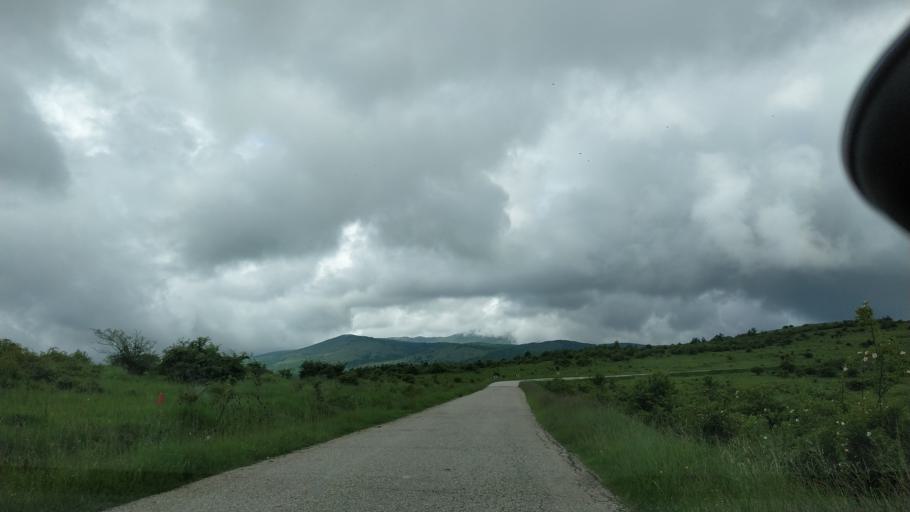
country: RS
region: Central Serbia
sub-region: Zajecarski Okrug
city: Soko Banja
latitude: 43.7051
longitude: 21.9375
